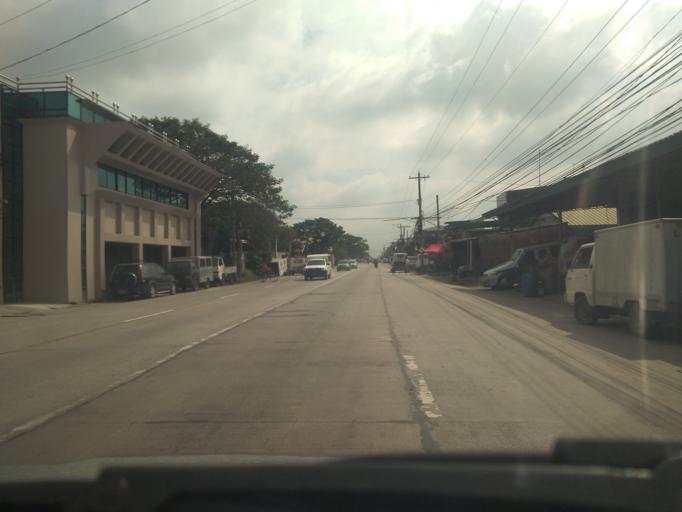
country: PH
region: Central Luzon
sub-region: Province of Pampanga
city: Santo Domingo
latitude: 15.0023
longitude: 120.7239
